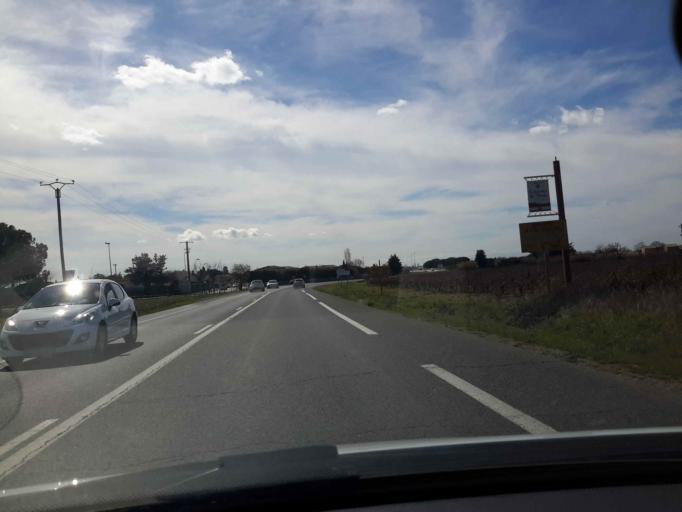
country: FR
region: Languedoc-Roussillon
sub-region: Departement du Gard
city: Aubord
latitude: 43.7624
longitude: 4.3165
